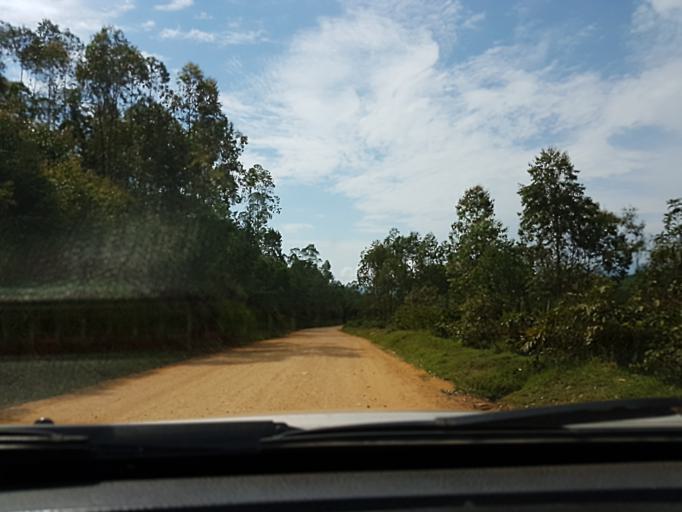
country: CD
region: South Kivu
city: Bukavu
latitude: -2.6274
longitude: 28.8745
